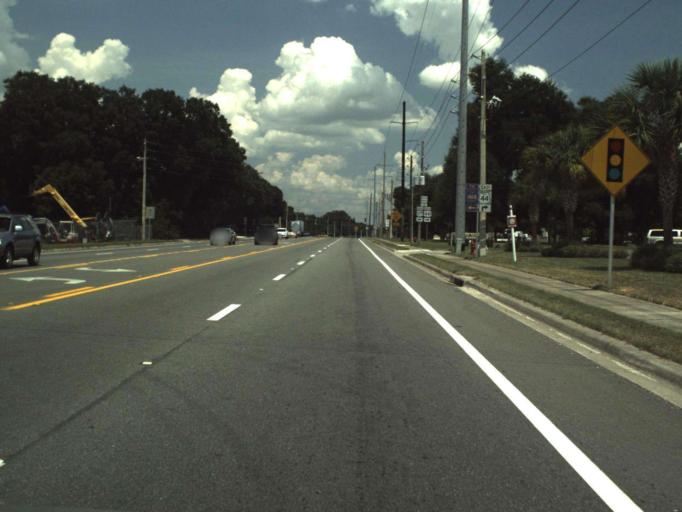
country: US
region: Florida
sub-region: Lake County
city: Leesburg
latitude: 28.8117
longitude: -81.9196
